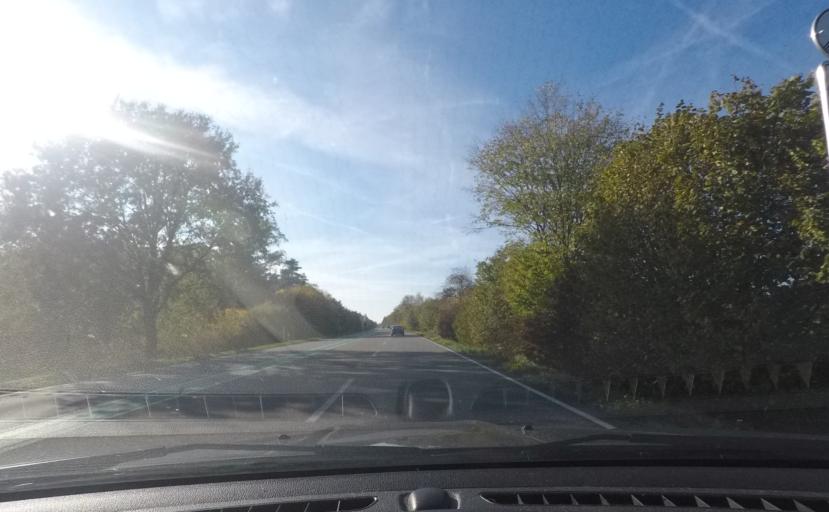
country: DE
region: North Rhine-Westphalia
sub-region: Regierungsbezirk Munster
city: Heiden
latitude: 51.8580
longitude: 6.9514
